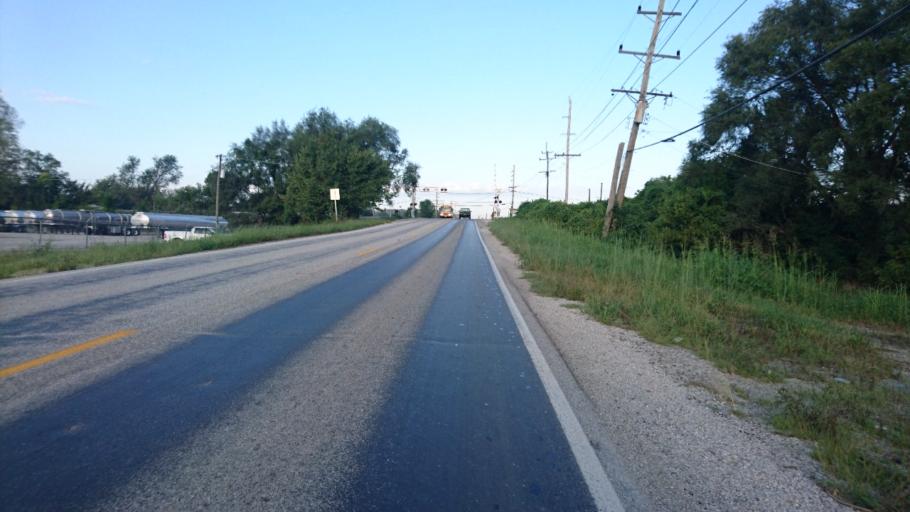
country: US
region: Illinois
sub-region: Madison County
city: Mitchell
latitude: 38.7621
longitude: -90.1160
